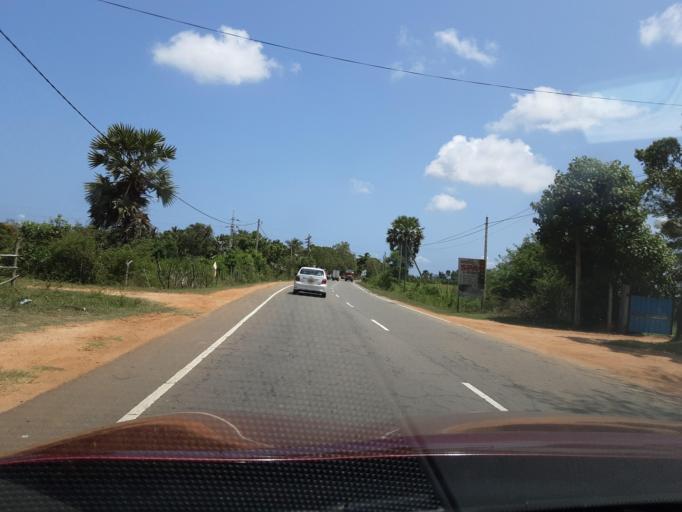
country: LK
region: Southern
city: Tangalla
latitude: 6.2370
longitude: 81.2275
